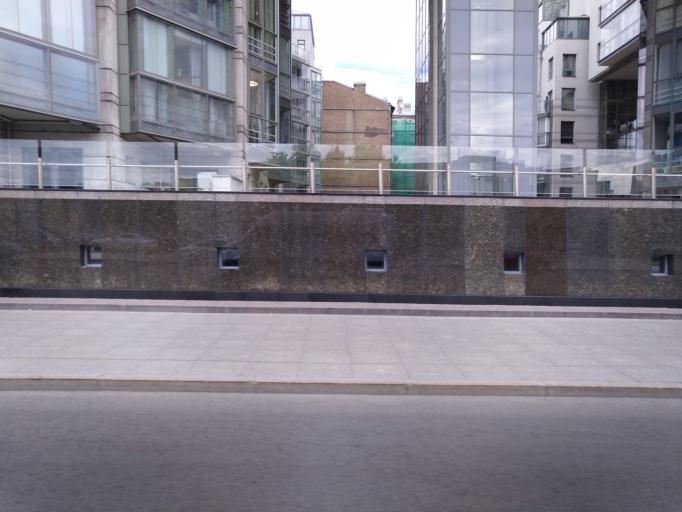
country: RU
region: Leningrad
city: Finlyandskiy
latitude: 59.9487
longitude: 30.3791
